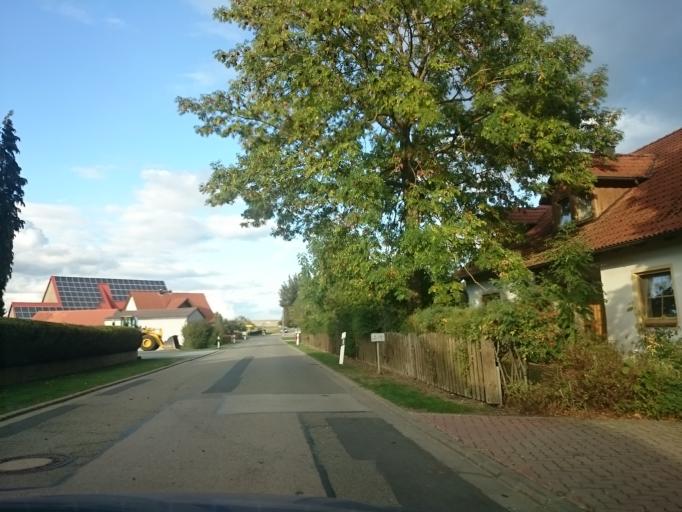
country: DE
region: Bavaria
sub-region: Regierungsbezirk Mittelfranken
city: Thalmassing
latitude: 49.0686
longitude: 11.1893
